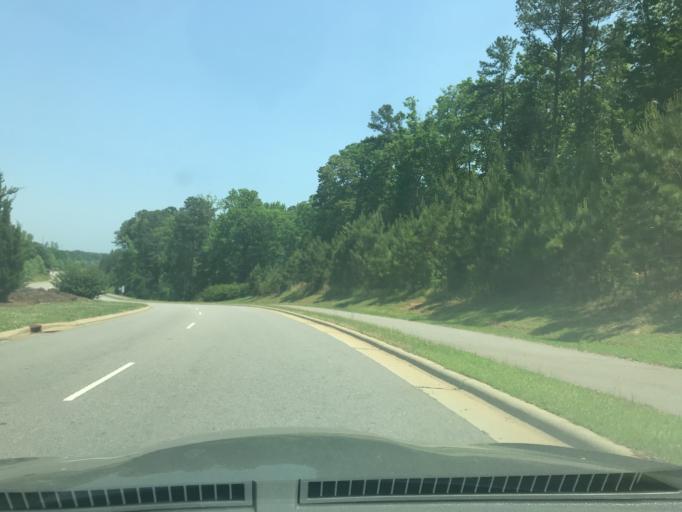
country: US
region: North Carolina
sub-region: Wake County
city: Cary
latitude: 35.7913
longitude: -78.7272
